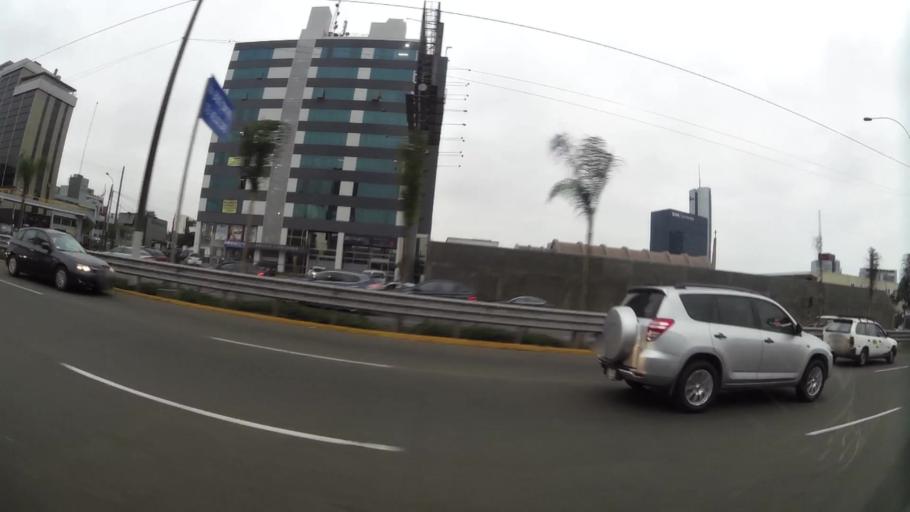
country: PE
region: Lima
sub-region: Lima
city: San Luis
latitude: -12.0902
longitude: -77.0197
